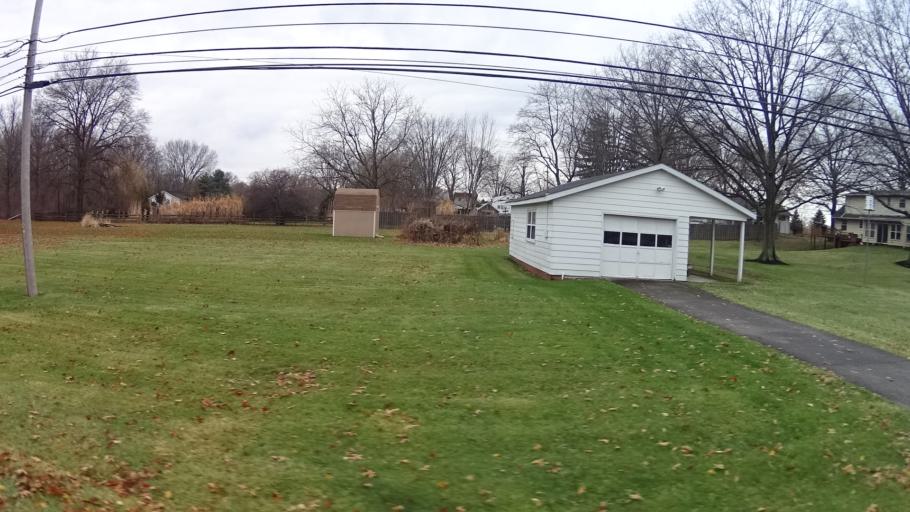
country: US
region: Ohio
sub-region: Lorain County
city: North Ridgeville
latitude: 41.3660
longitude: -82.0562
